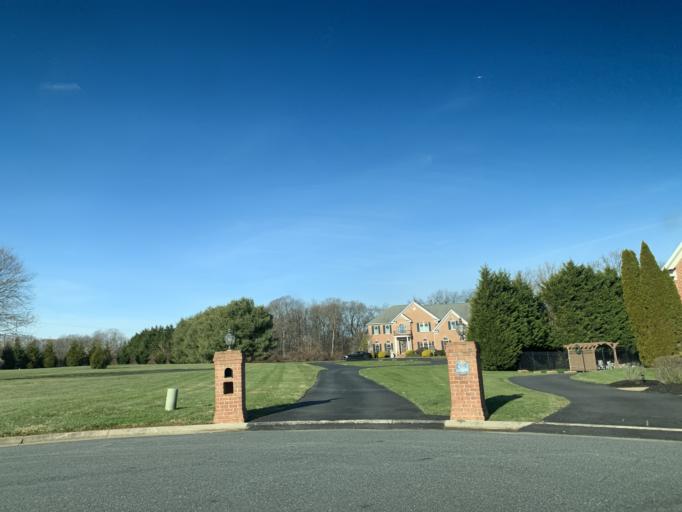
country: US
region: Maryland
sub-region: Harford County
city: South Bel Air
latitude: 39.5704
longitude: -76.2529
